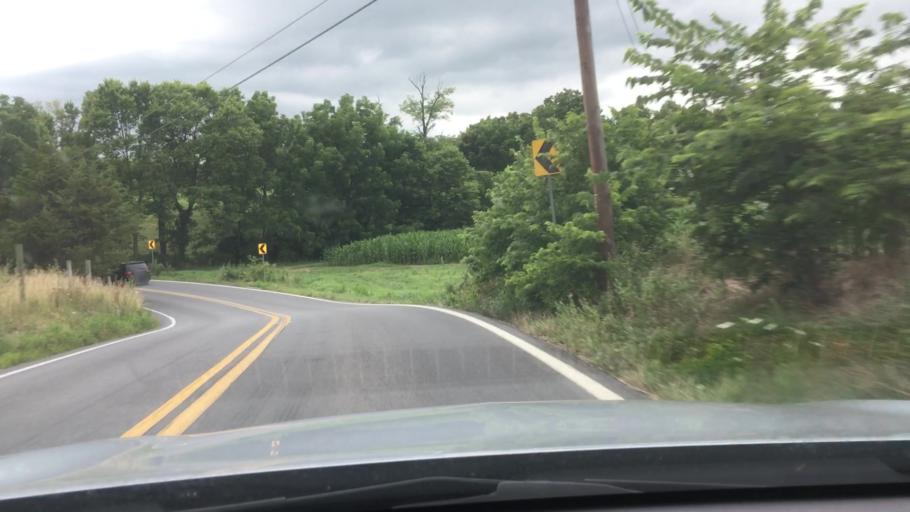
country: US
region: Pennsylvania
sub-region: Franklin County
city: Greencastle
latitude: 39.8640
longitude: -77.7949
